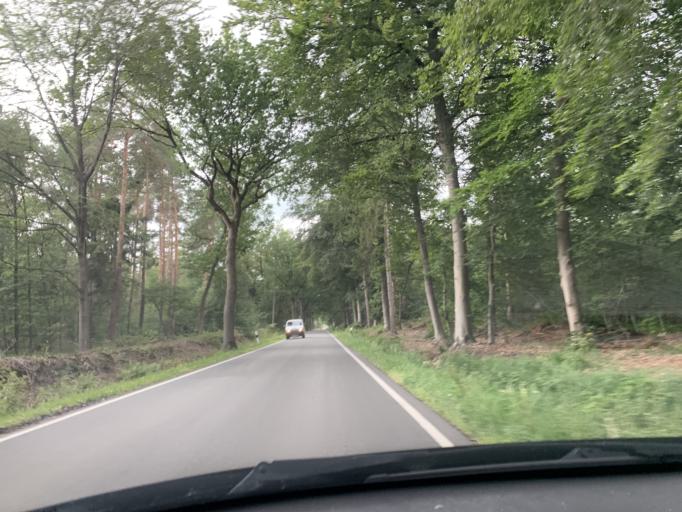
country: DE
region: Lower Saxony
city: Westerstede
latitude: 53.2190
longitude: 7.9123
